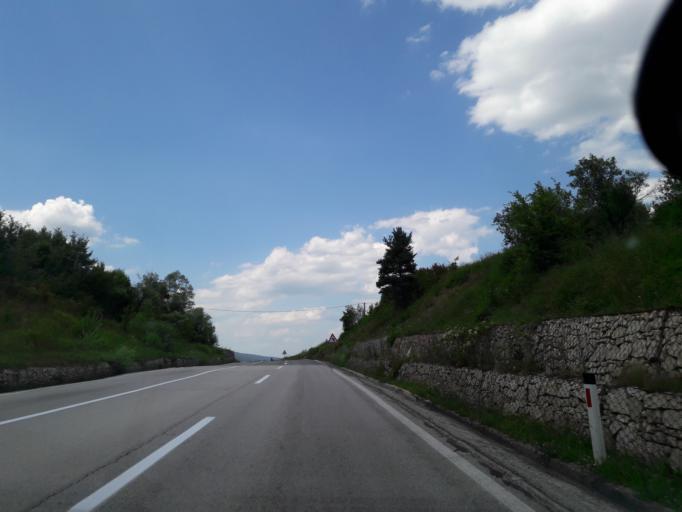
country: BA
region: Republika Srpska
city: Mrkonjic Grad
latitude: 44.4863
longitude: 17.1620
